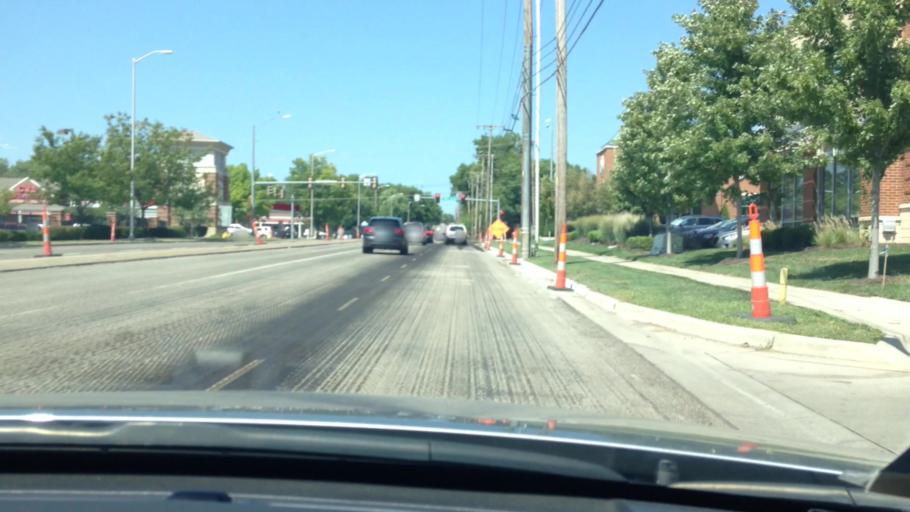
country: US
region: Kansas
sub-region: Johnson County
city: Overland Park
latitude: 38.9557
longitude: -94.6862
